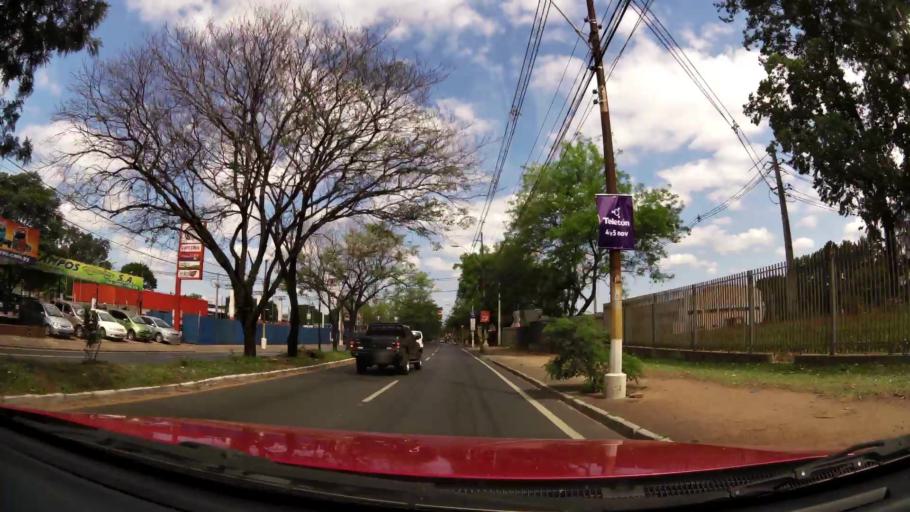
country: PY
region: Central
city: Fernando de la Mora
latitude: -25.3289
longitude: -57.5177
